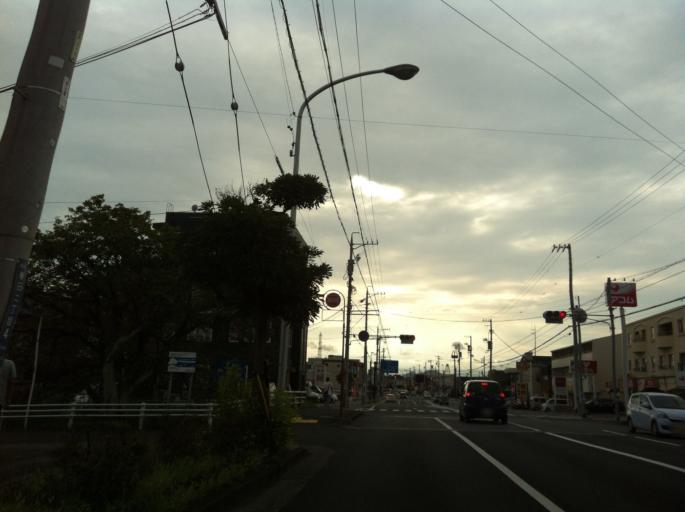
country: JP
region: Shizuoka
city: Shizuoka-shi
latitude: 35.0111
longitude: 138.4713
